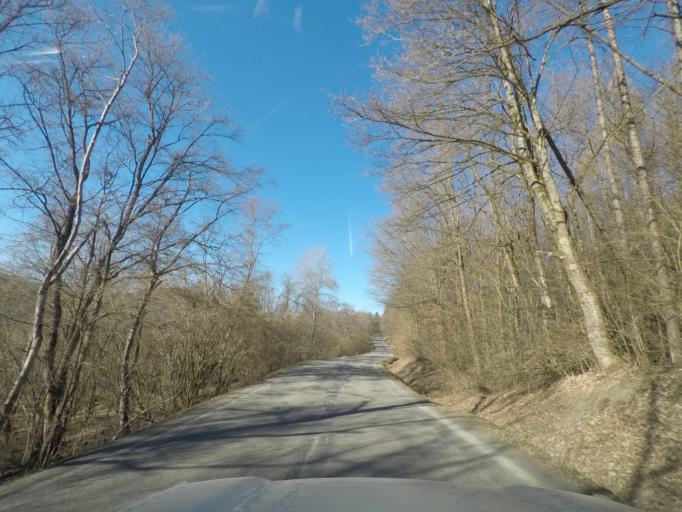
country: SK
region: Presovsky
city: Snina
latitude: 49.0346
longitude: 22.1730
